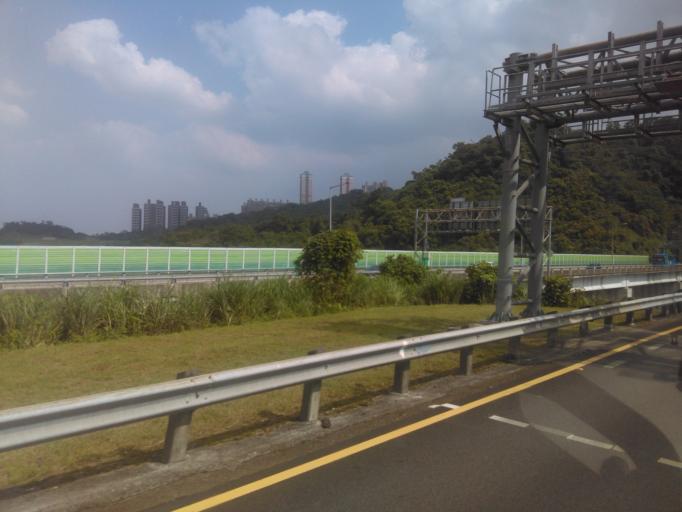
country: TW
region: Taipei
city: Taipei
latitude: 25.0352
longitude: 121.6230
